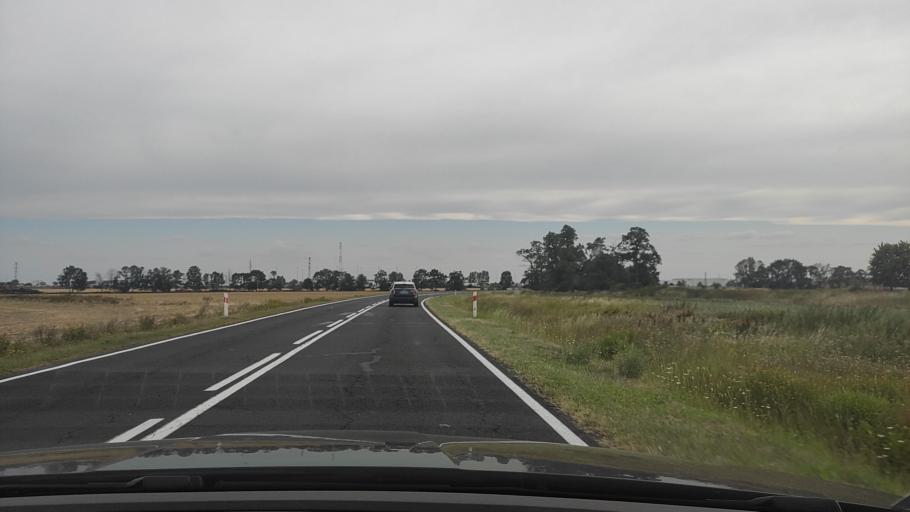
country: PL
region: Greater Poland Voivodeship
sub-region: Powiat poznanski
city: Kleszczewo
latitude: 52.3179
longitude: 17.1519
